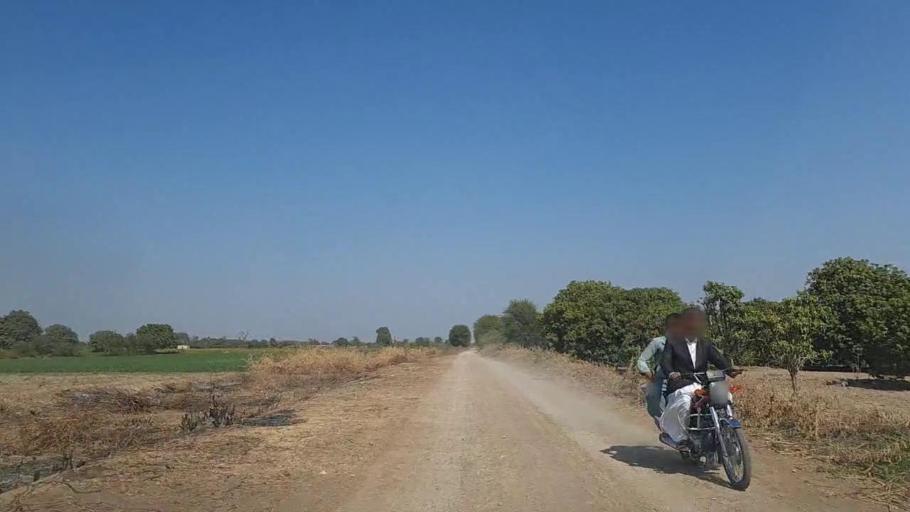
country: PK
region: Sindh
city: Digri
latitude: 25.1318
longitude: 69.1463
